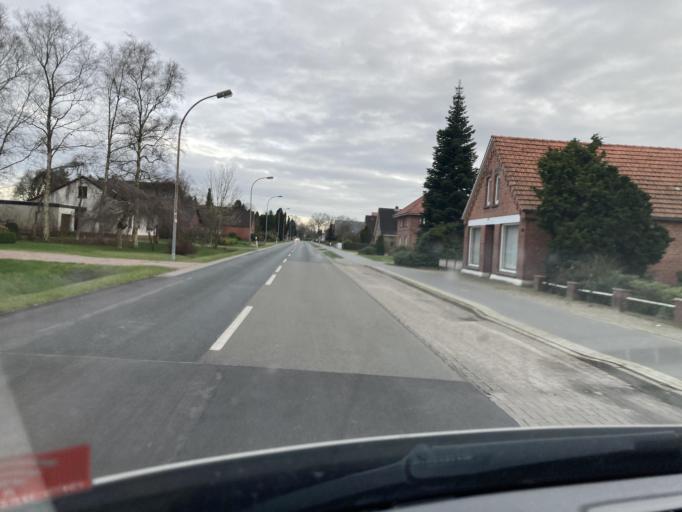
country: DE
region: Lower Saxony
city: Leer
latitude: 53.1508
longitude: 7.4710
